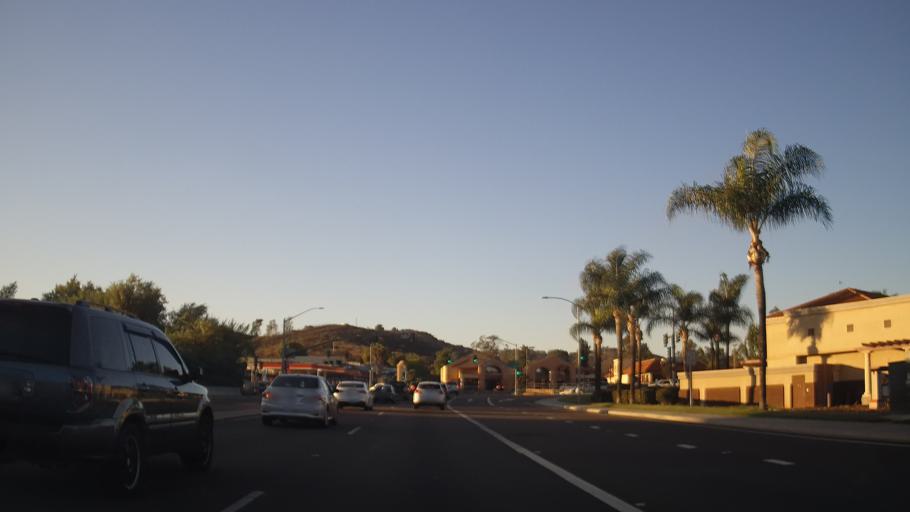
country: US
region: California
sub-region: San Diego County
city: Rancho San Diego
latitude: 32.7386
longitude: -116.9420
